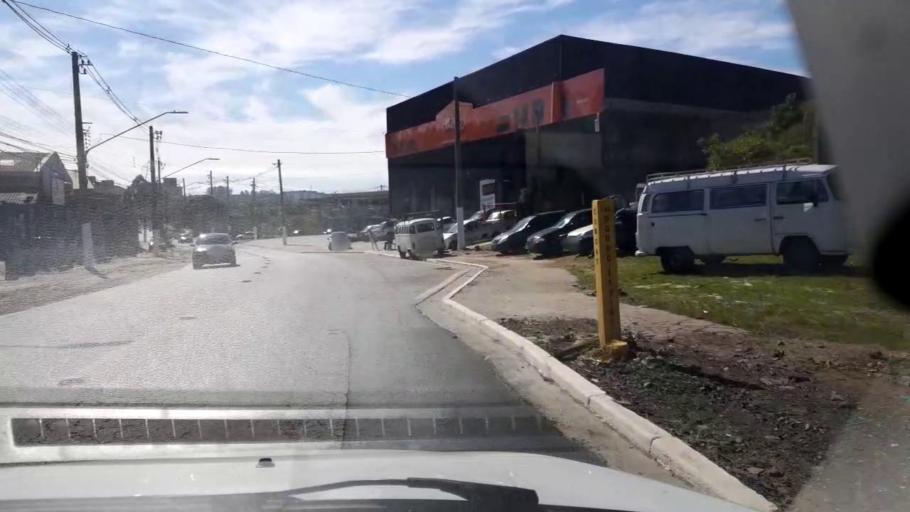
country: BR
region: Sao Paulo
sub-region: Ferraz De Vasconcelos
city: Ferraz de Vasconcelos
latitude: -23.5755
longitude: -46.4161
